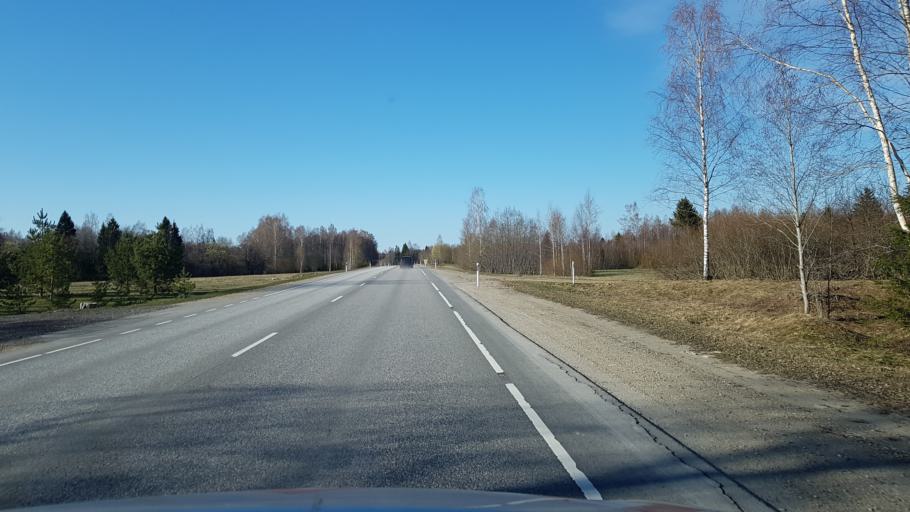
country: EE
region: Ida-Virumaa
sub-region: Johvi vald
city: Johvi
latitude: 59.1964
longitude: 27.3463
